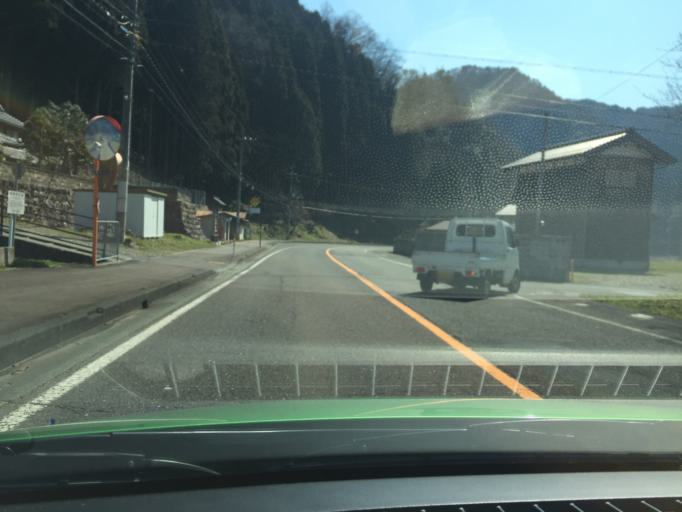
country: JP
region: Fukui
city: Obama
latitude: 35.3962
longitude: 135.5935
